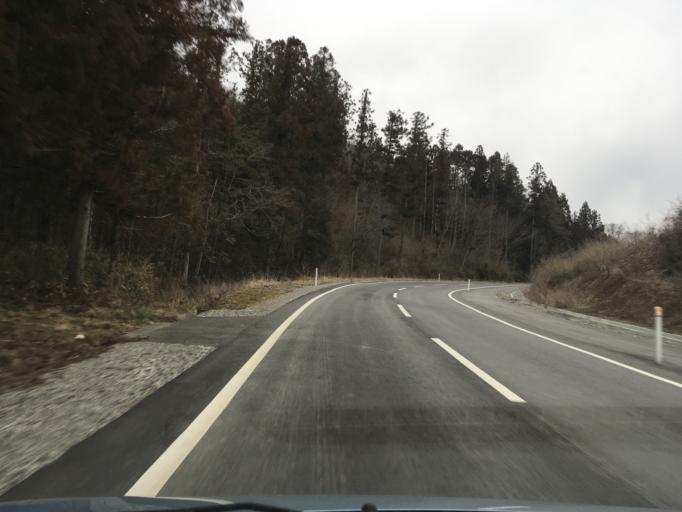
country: JP
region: Miyagi
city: Wakuya
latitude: 38.6703
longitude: 141.2759
